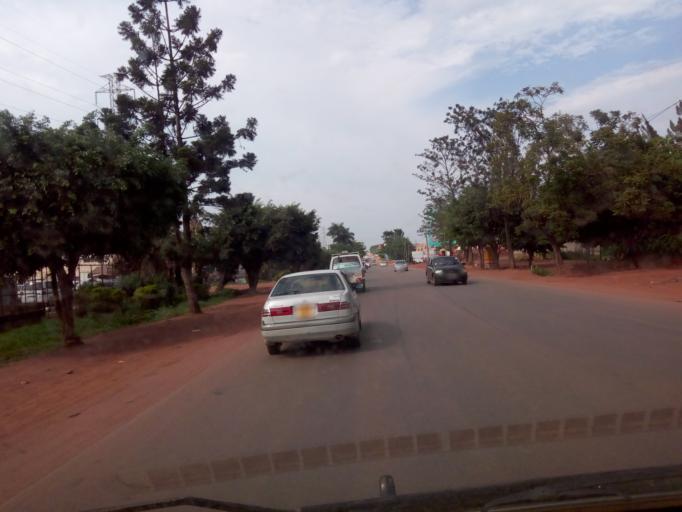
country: UG
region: Central Region
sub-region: Wakiso District
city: Kireka
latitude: 0.3379
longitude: 32.6244
